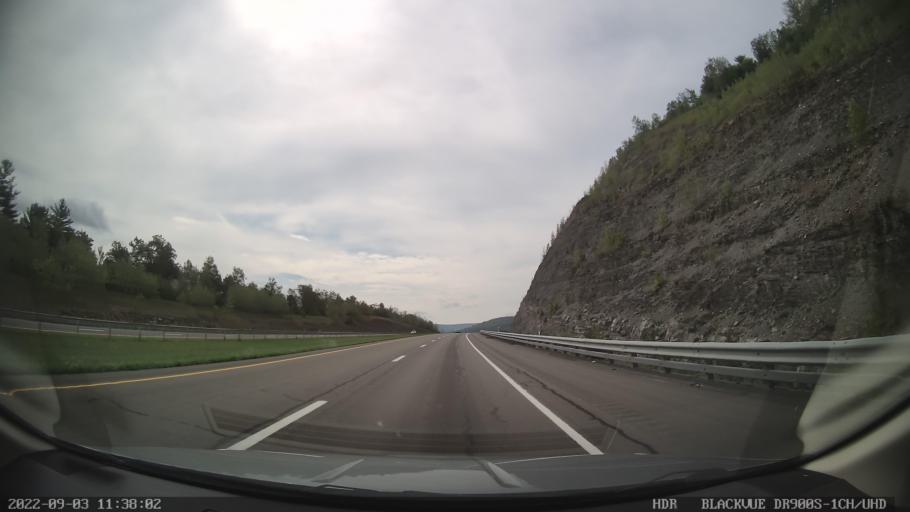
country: US
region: Pennsylvania
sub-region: Tioga County
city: Mansfield
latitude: 41.9686
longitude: -77.1209
